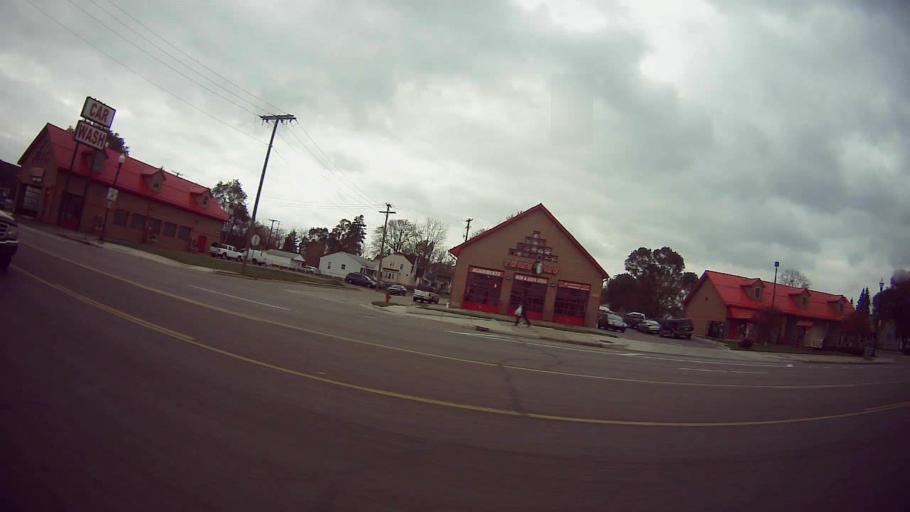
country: US
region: Michigan
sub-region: Macomb County
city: Warren
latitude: 42.4502
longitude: -83.0250
